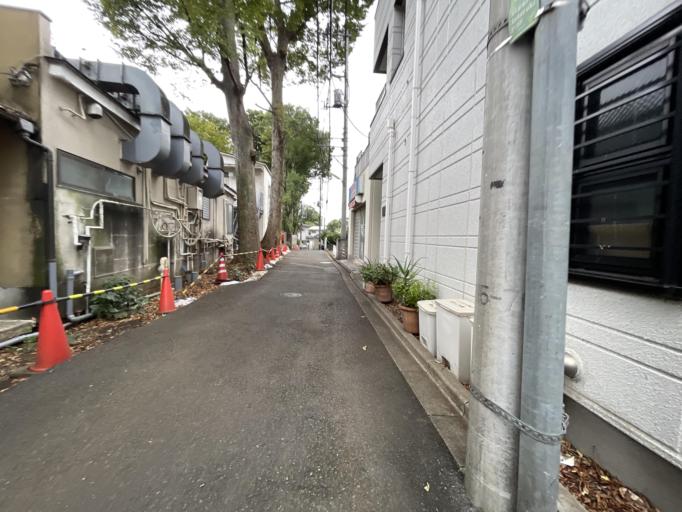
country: JP
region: Tokyo
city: Tokyo
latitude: 35.6085
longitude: 139.6470
